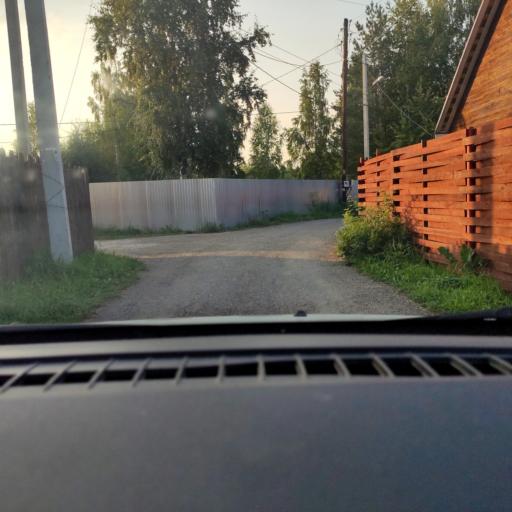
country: RU
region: Perm
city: Perm
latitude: 58.0330
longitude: 56.2308
